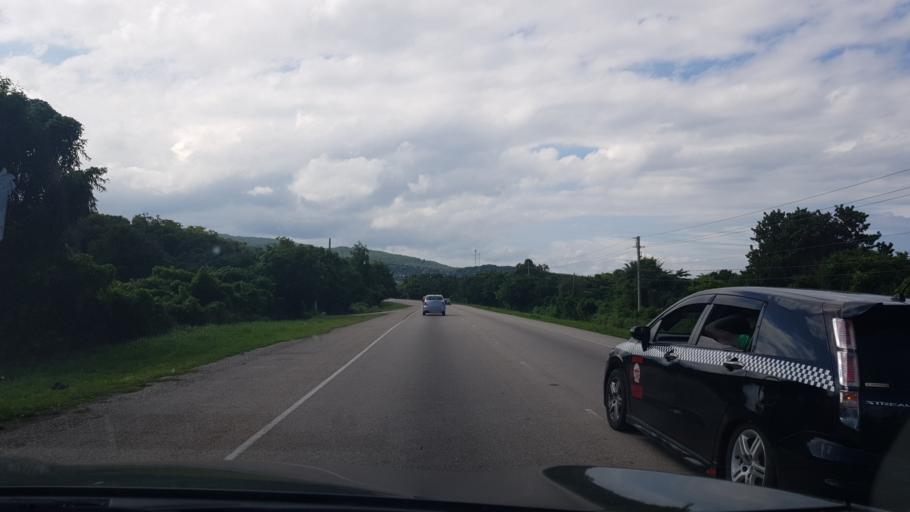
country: JM
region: Saint Ann
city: Discovery Bay
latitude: 18.4759
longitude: -77.4469
